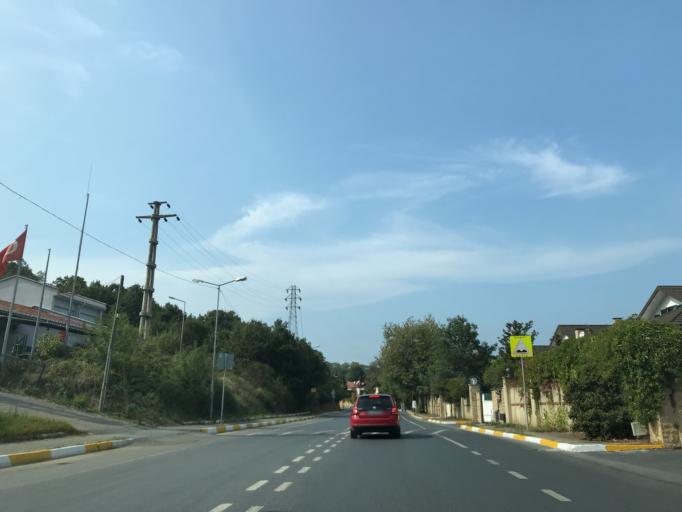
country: TR
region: Istanbul
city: Arikoey
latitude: 41.2426
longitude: 29.0409
